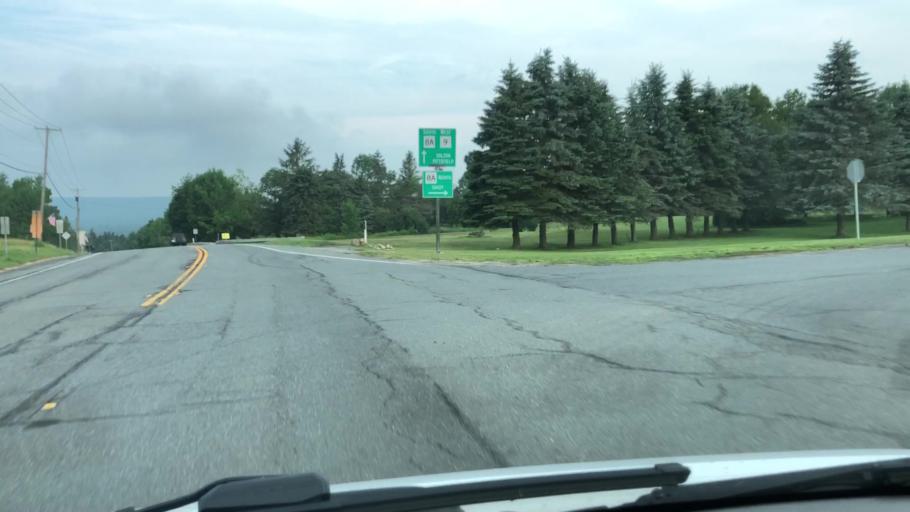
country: US
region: Massachusetts
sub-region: Berkshire County
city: Hinsdale
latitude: 42.5115
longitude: -73.0582
